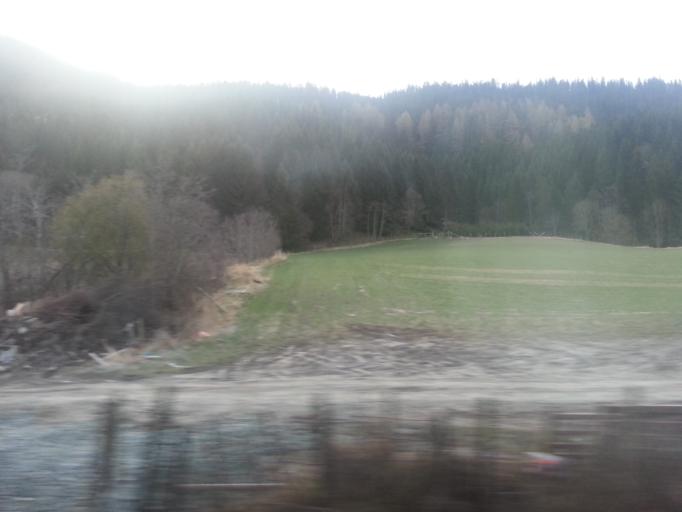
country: NO
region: Sor-Trondelag
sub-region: Melhus
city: Melhus
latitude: 63.2400
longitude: 10.2817
